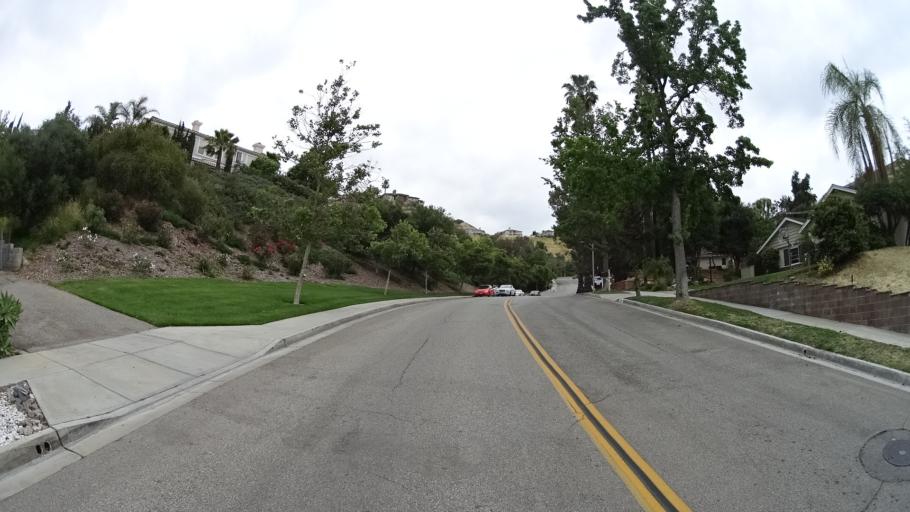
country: US
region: California
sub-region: Los Angeles County
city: Burbank
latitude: 34.2144
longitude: -118.3309
